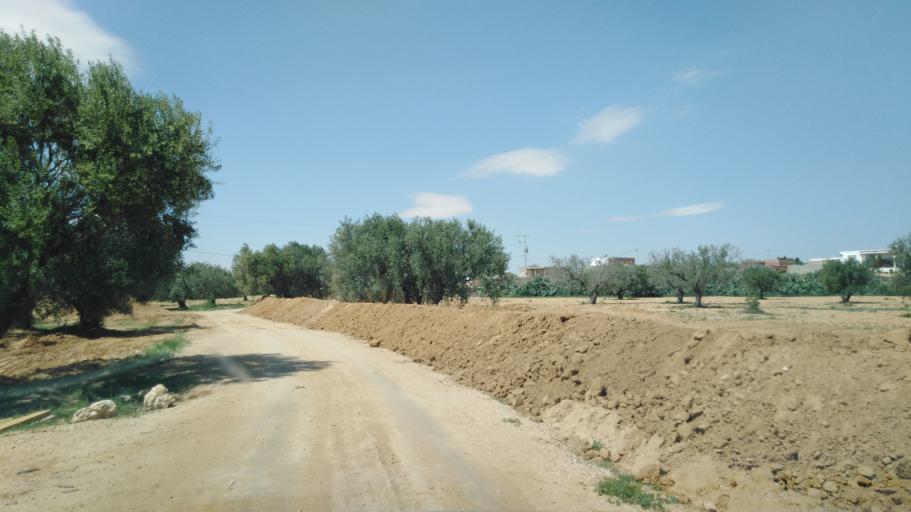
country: TN
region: Safaqis
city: Sfax
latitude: 34.7631
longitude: 10.5234
